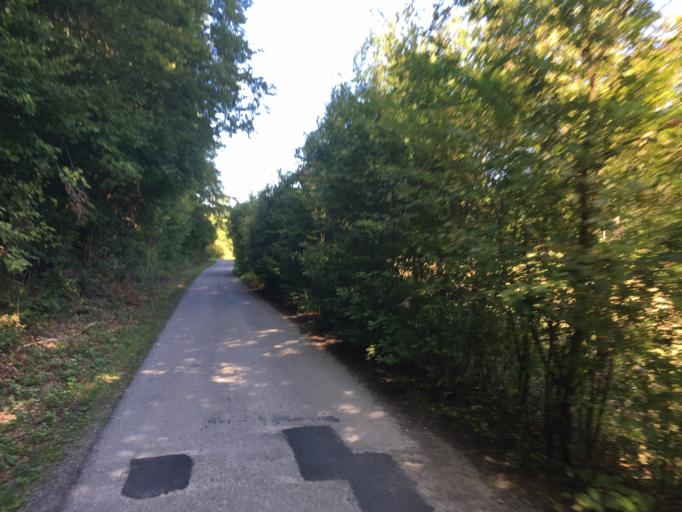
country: SK
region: Trenciansky
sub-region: Okres Povazska Bystrica
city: Povazska Bystrica
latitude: 49.0276
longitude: 18.4357
